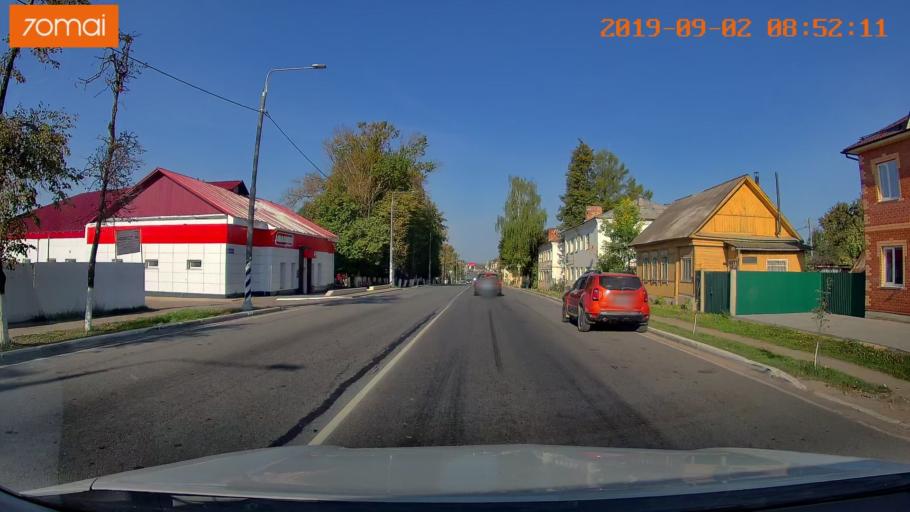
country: RU
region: Kaluga
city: Medyn'
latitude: 54.9666
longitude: 35.8650
